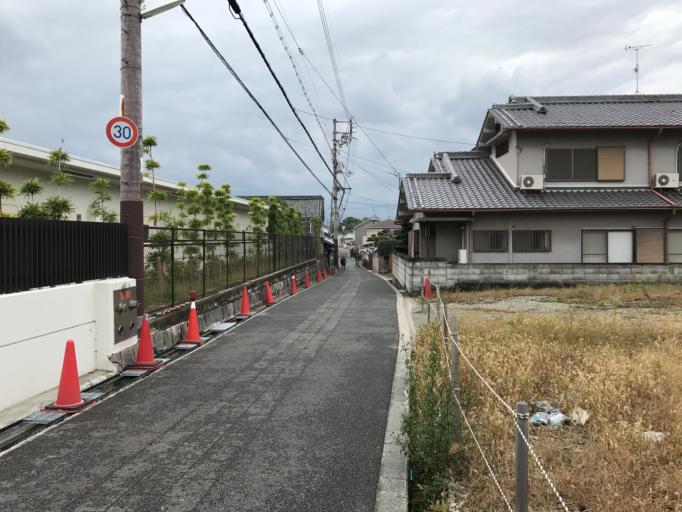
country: JP
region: Osaka
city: Kashihara
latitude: 34.5614
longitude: 135.6122
